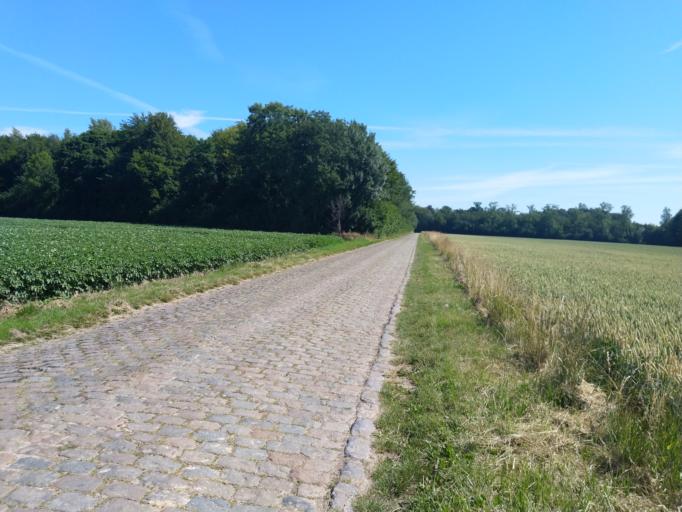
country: FR
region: Nord-Pas-de-Calais
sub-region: Departement du Nord
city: La Longueville
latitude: 50.3502
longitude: 3.8603
